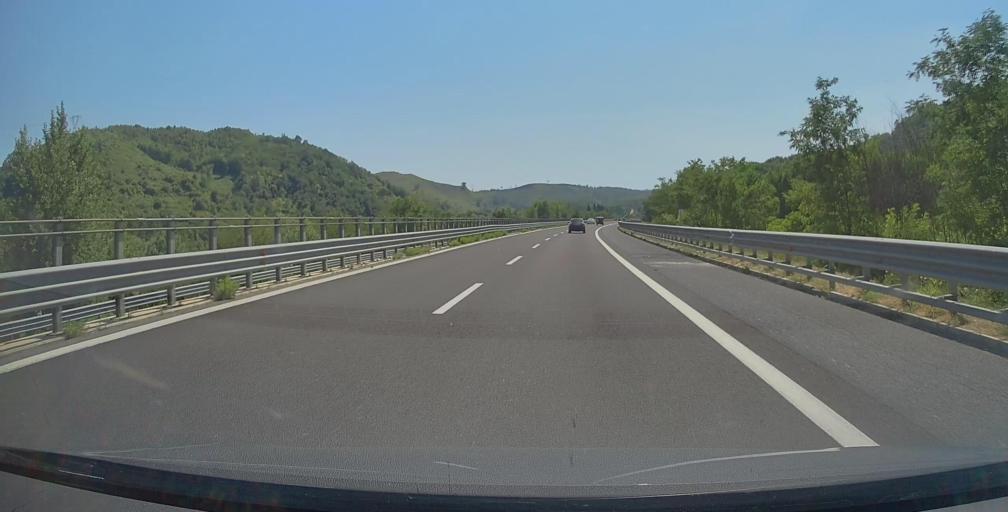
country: IT
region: Calabria
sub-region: Provincia di Vibo-Valentia
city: Francica
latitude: 38.5825
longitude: 16.1320
